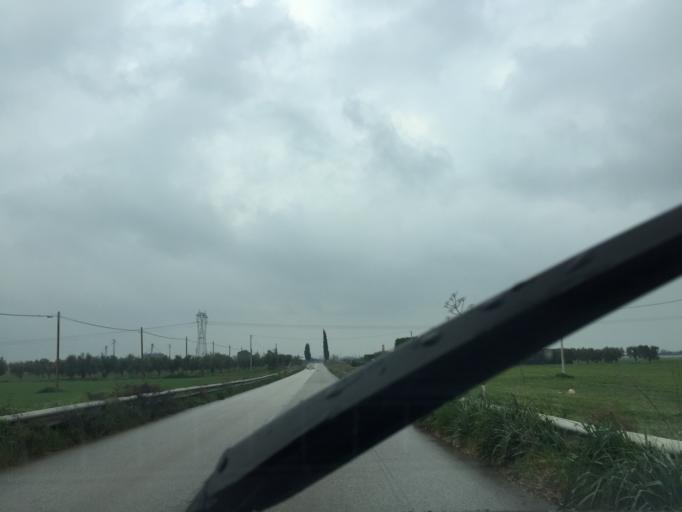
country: IT
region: Apulia
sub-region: Provincia di Foggia
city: Foggia
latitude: 41.4343
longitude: 15.4802
